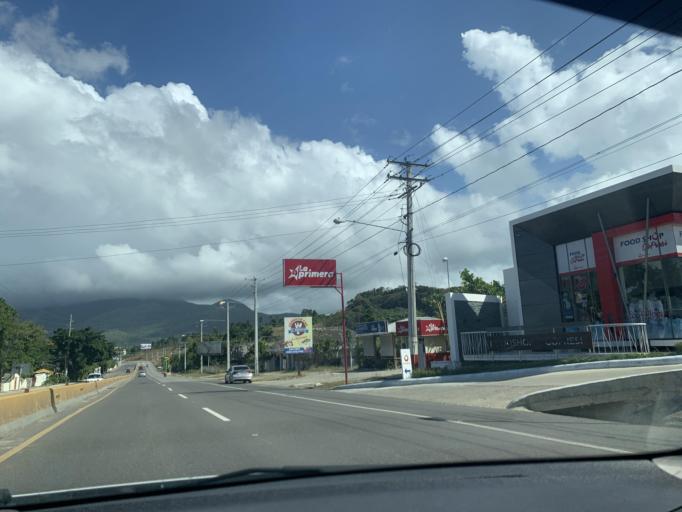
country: DO
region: Puerto Plata
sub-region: Puerto Plata
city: Puerto Plata
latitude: 19.8119
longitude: -70.7309
